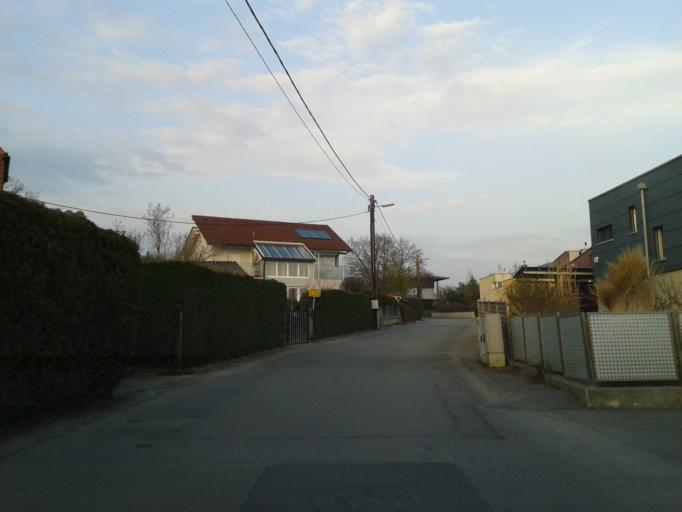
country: AT
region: Styria
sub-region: Politischer Bezirk Graz-Umgebung
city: Stattegg
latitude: 47.1206
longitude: 15.4301
